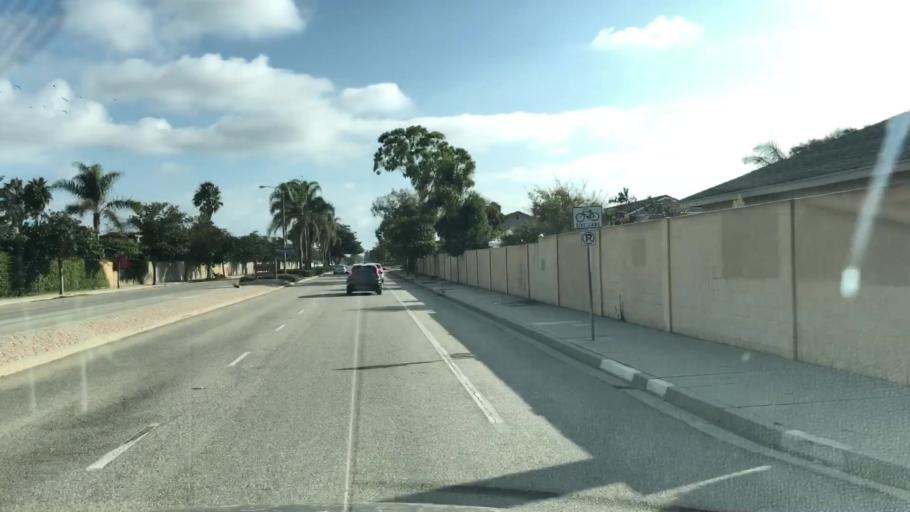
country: US
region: California
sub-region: Ventura County
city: Oxnard
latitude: 34.1934
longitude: -119.2081
